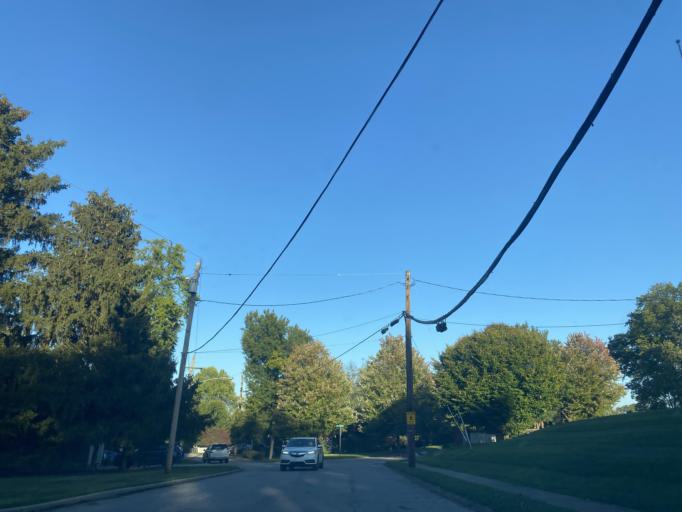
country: US
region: Kentucky
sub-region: Campbell County
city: Fort Thomas
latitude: 39.0995
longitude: -84.4493
